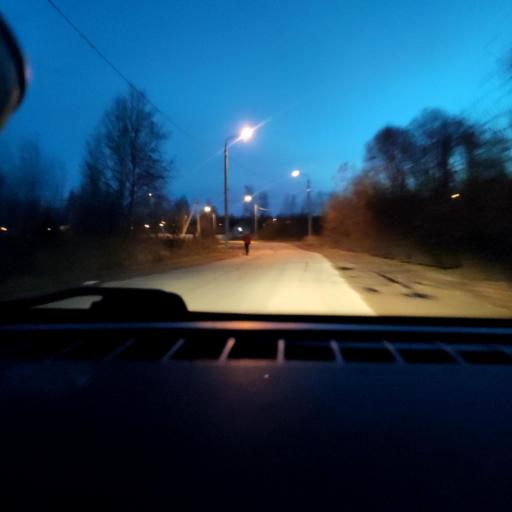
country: RU
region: Perm
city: Kondratovo
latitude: 58.0239
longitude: 56.1669
